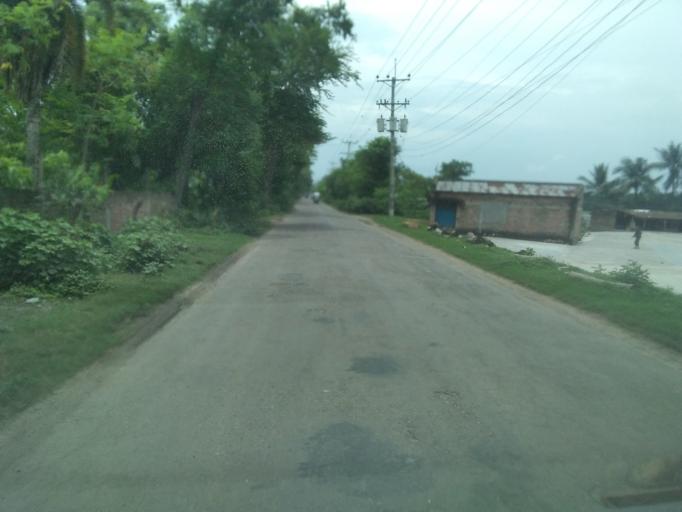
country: IN
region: West Bengal
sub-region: North 24 Parganas
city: Taki
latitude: 22.5710
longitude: 89.0009
